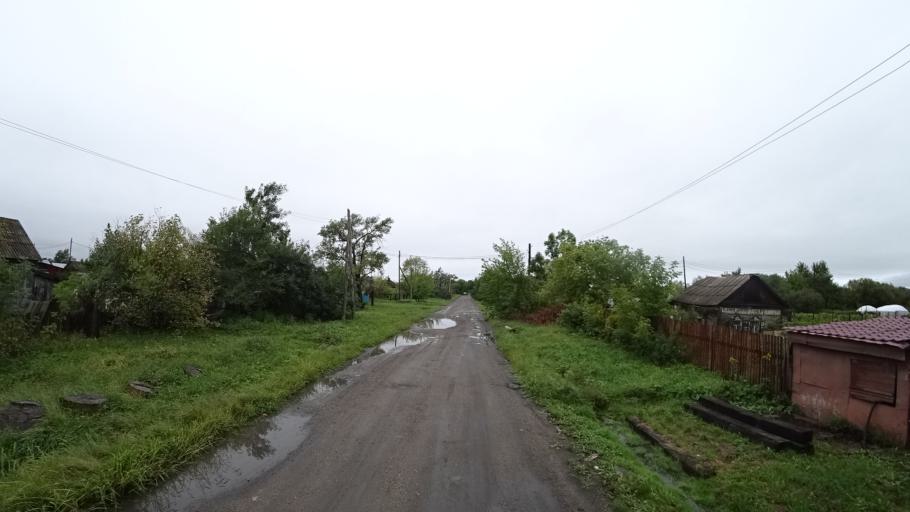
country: RU
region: Primorskiy
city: Monastyrishche
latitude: 44.2117
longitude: 132.4315
